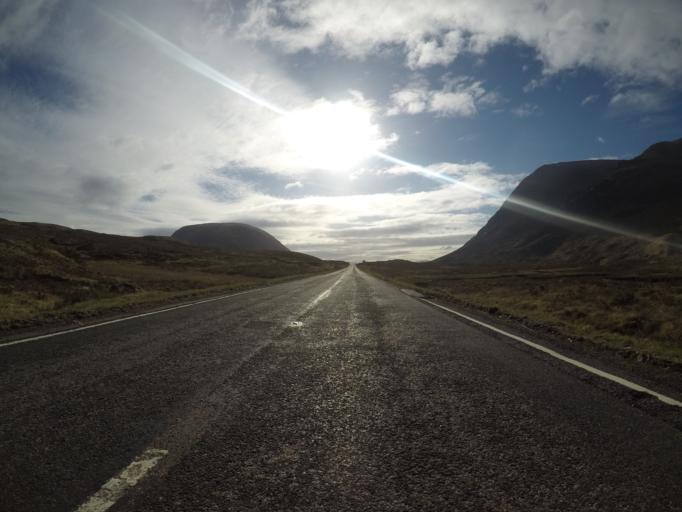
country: GB
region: Scotland
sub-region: Highland
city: Spean Bridge
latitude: 56.6622
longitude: -4.9238
